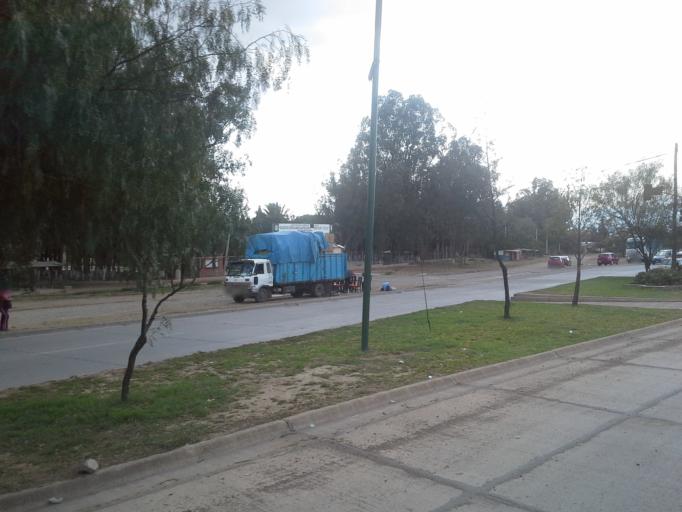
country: BO
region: Cochabamba
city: Cochabamba
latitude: -17.4474
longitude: -66.1342
